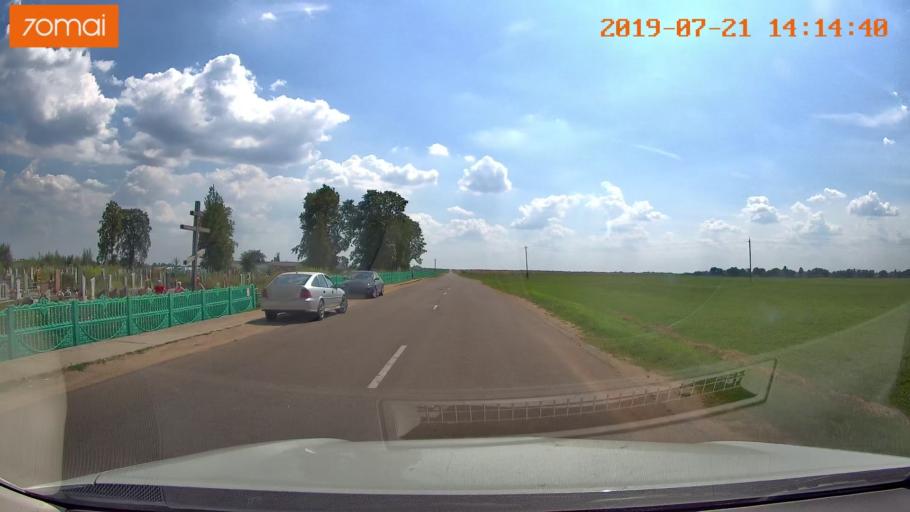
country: BY
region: Grodnenskaya
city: Karelichy
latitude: 53.6449
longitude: 26.1679
